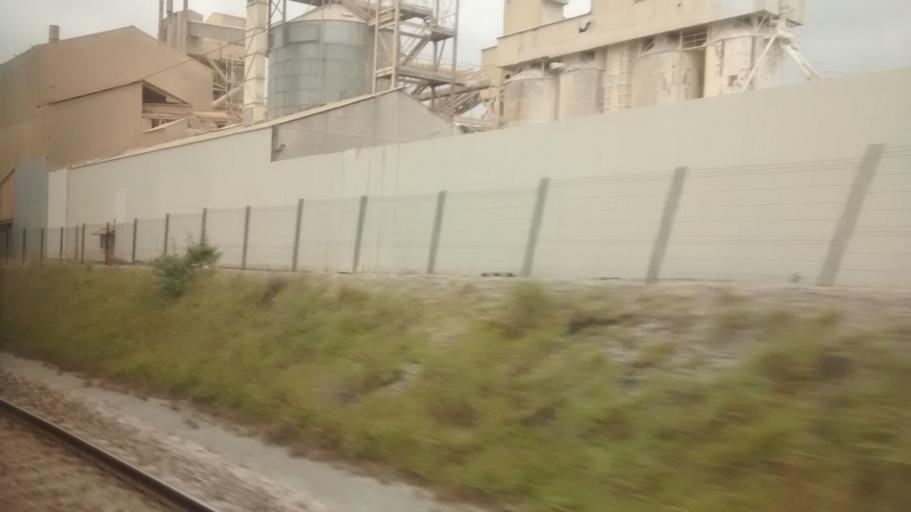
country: FR
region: Pays de la Loire
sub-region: Departement de la Mayenne
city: Evron
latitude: 48.1586
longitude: -0.4641
